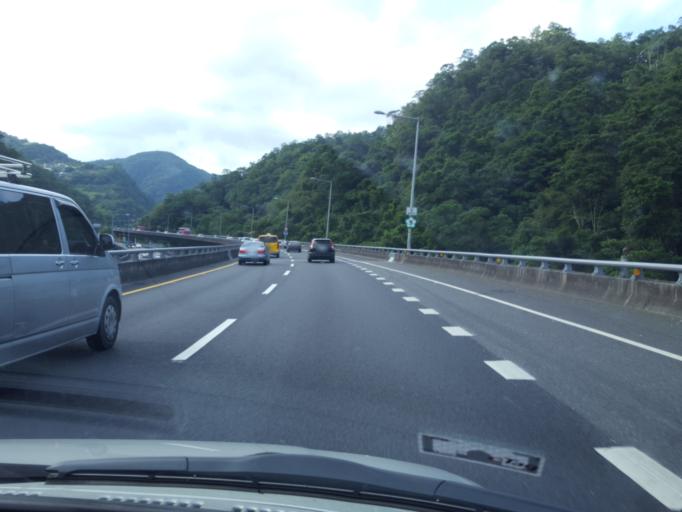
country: TW
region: Taiwan
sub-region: Keelung
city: Keelung
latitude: 24.9449
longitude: 121.7106
